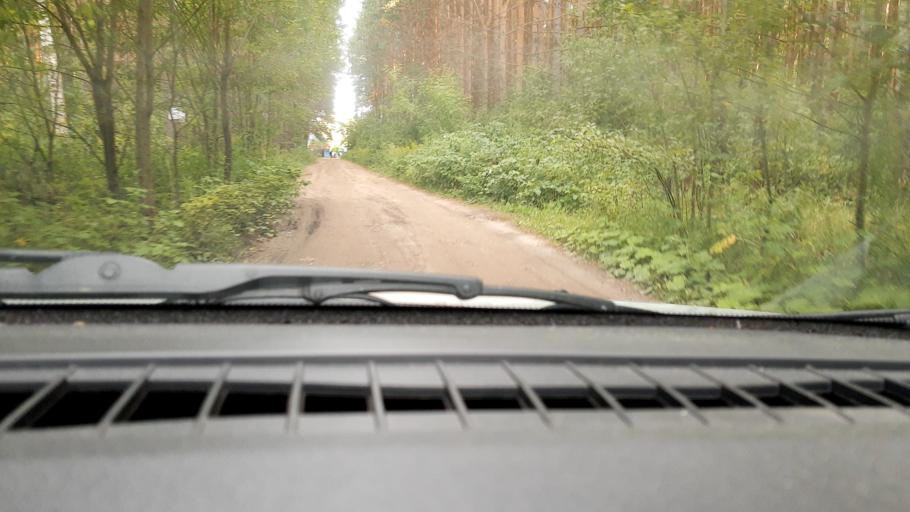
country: RU
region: Nizjnij Novgorod
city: Sitniki
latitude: 56.4513
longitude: 44.0201
